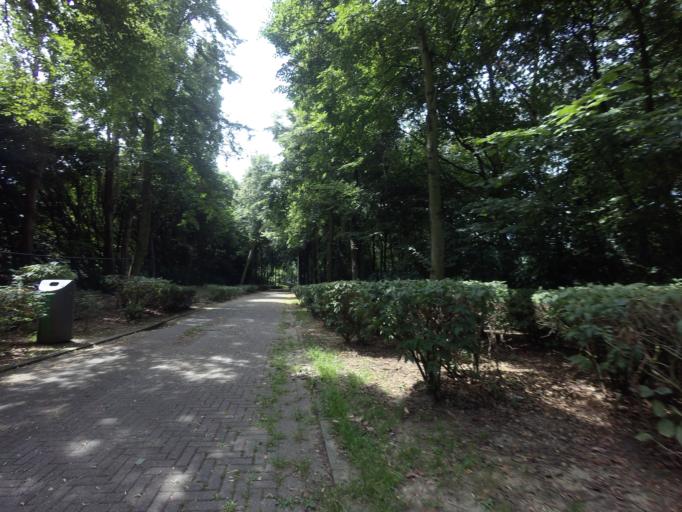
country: BE
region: Flanders
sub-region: Provincie Antwerpen
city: Mortsel
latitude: 51.1857
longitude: 4.4403
